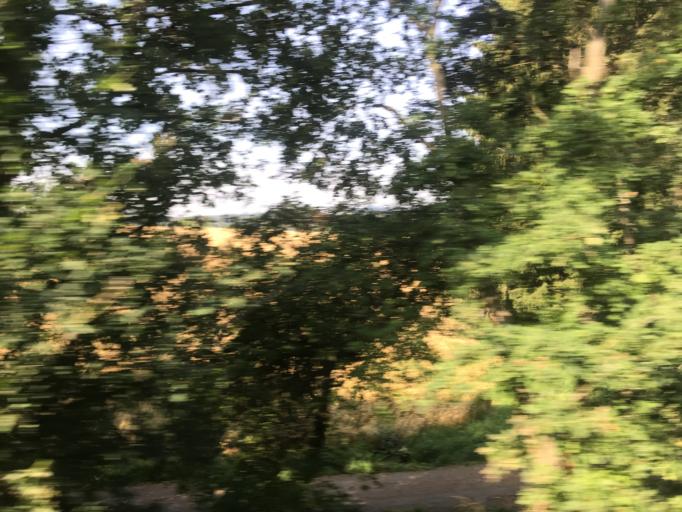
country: CZ
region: Jihocesky
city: Chotoviny
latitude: 49.5182
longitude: 14.6669
